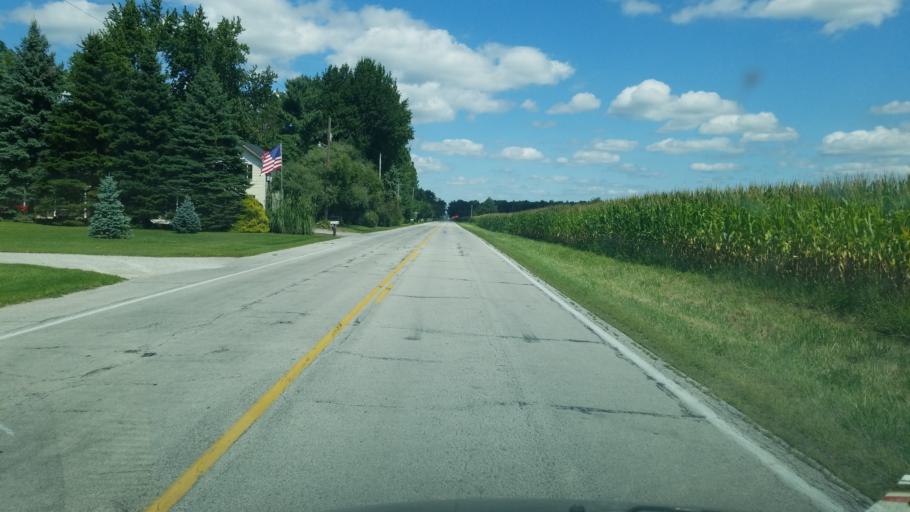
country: US
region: Ohio
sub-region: Lucas County
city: Whitehouse
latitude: 41.4448
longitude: -83.8736
